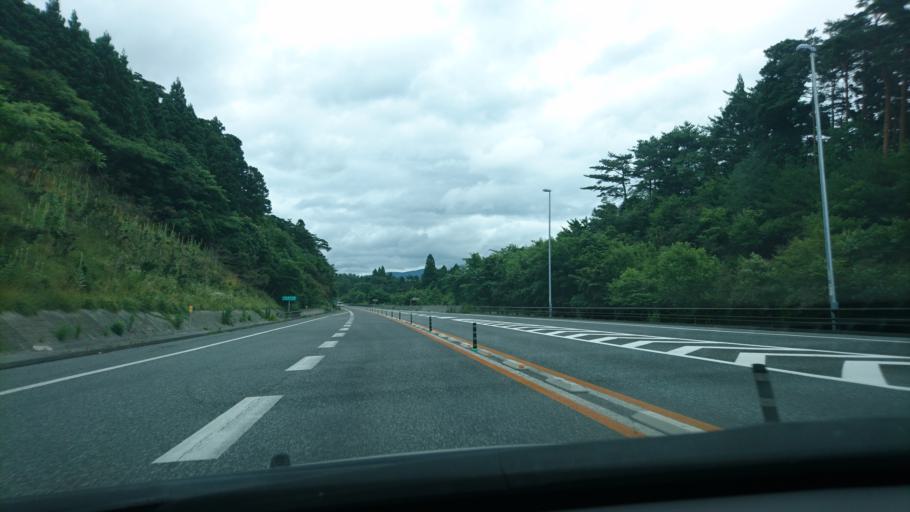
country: JP
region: Iwate
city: Ofunato
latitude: 39.0364
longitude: 141.7140
